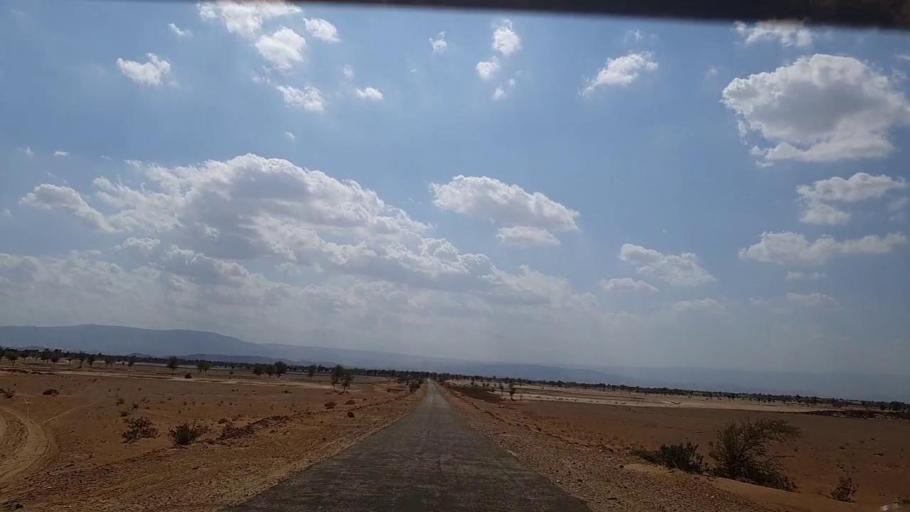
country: PK
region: Sindh
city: Johi
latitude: 26.5218
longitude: 67.4999
